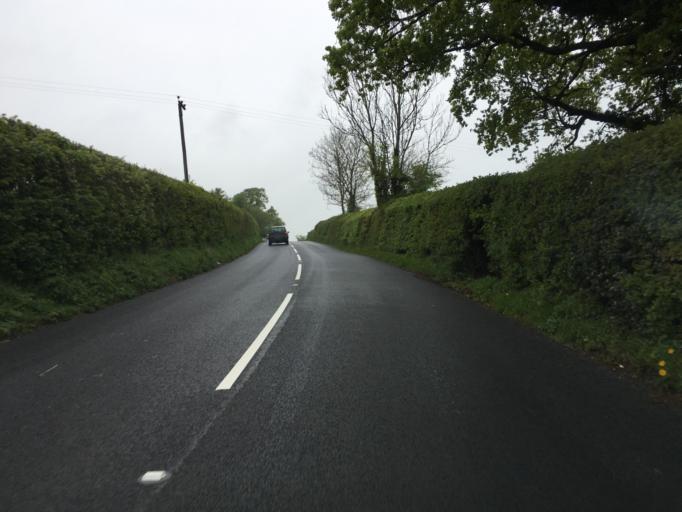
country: GB
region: England
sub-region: North Somerset
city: Blagdon
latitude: 51.3226
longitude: -2.6938
